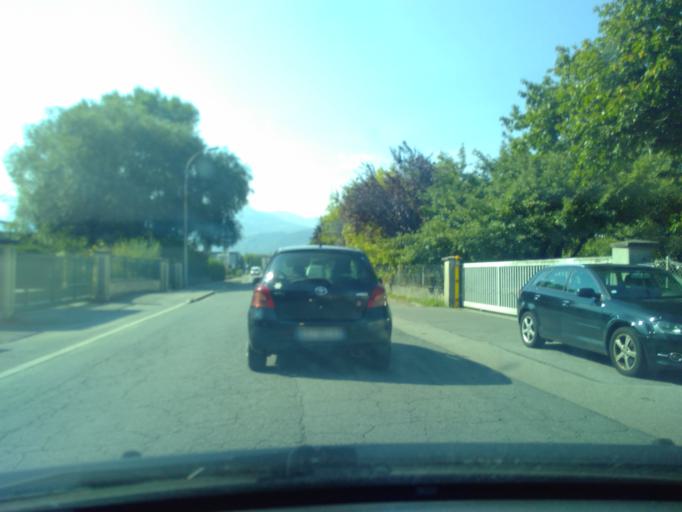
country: FR
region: Rhone-Alpes
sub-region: Departement de la Haute-Savoie
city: Sallanches
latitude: 45.9531
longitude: 6.6314
